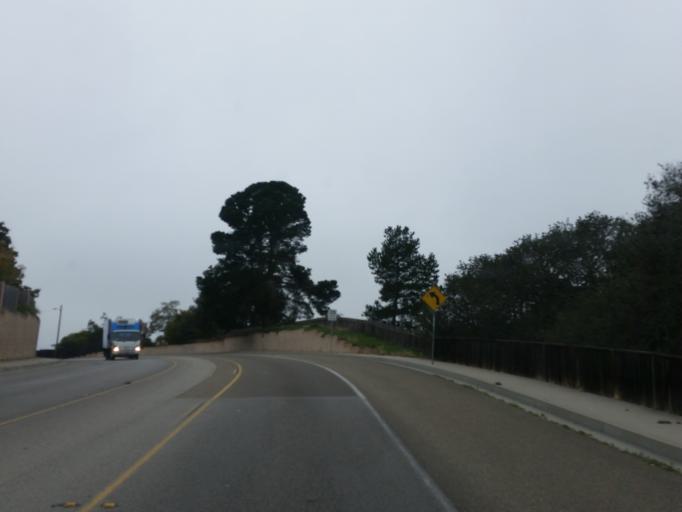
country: US
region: California
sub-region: San Luis Obispo County
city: Grover Beach
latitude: 35.1308
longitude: -120.6249
